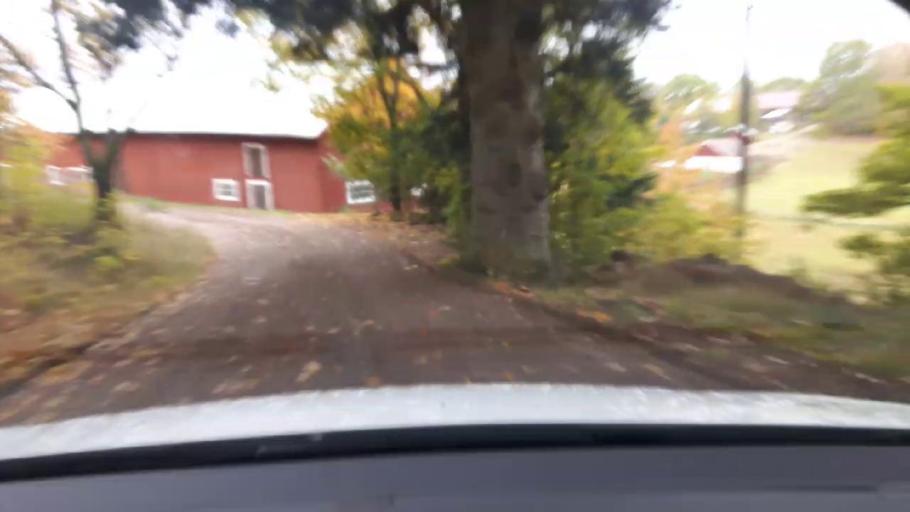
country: SE
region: Kalmar
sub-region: Vimmerby Kommun
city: Sodra Vi
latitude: 57.9553
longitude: 15.8975
